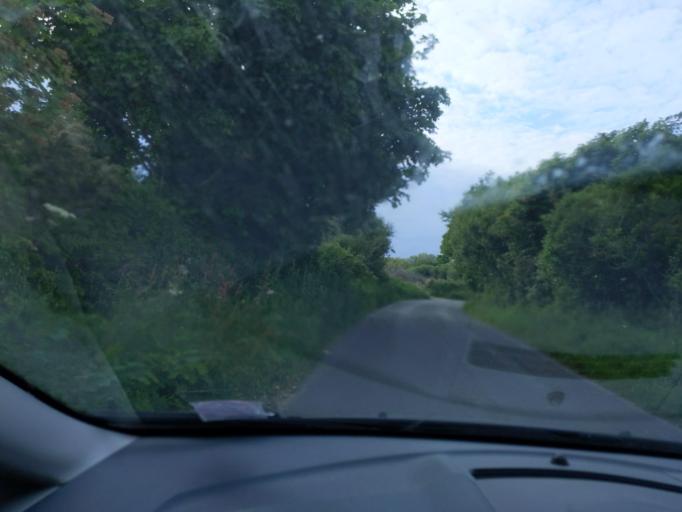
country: IM
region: Ramsey
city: Ramsey
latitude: 54.3490
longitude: -4.4498
